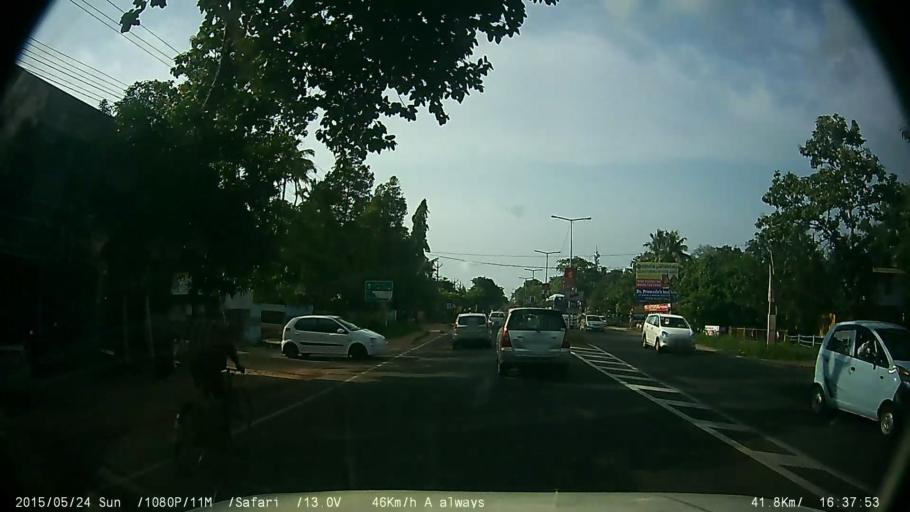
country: IN
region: Kerala
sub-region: Alappuzha
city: Shertallai
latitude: 9.6067
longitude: 76.3292
